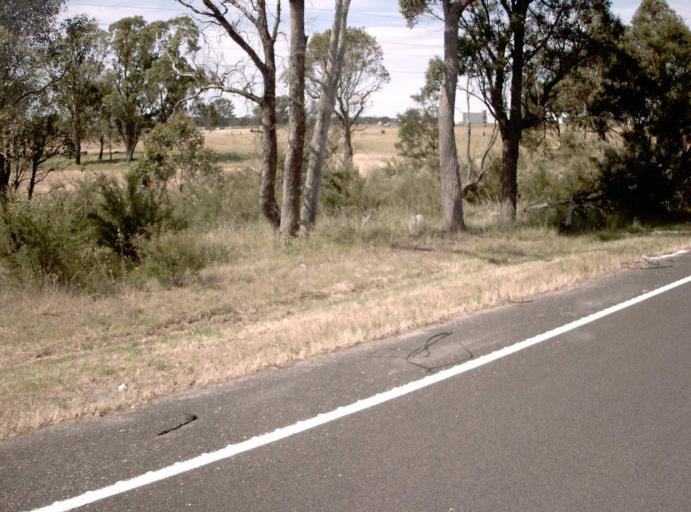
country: AU
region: Victoria
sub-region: Wellington
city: Sale
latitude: -37.9295
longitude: 147.2036
